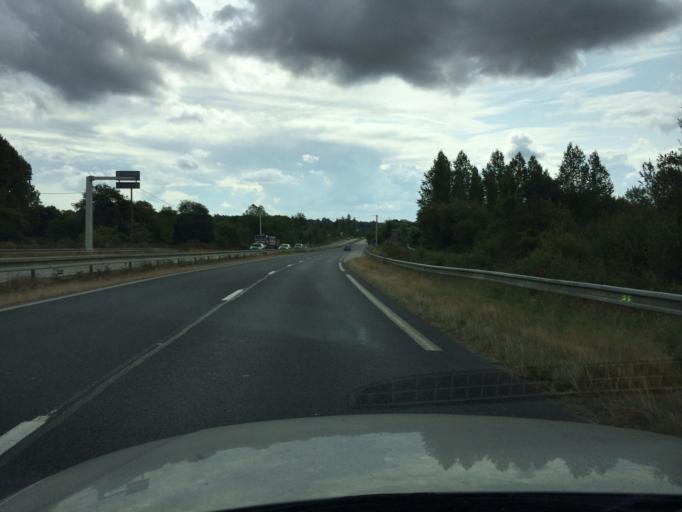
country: FR
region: Lower Normandy
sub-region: Departement de la Manche
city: Valognes
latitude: 49.5312
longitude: -1.5233
